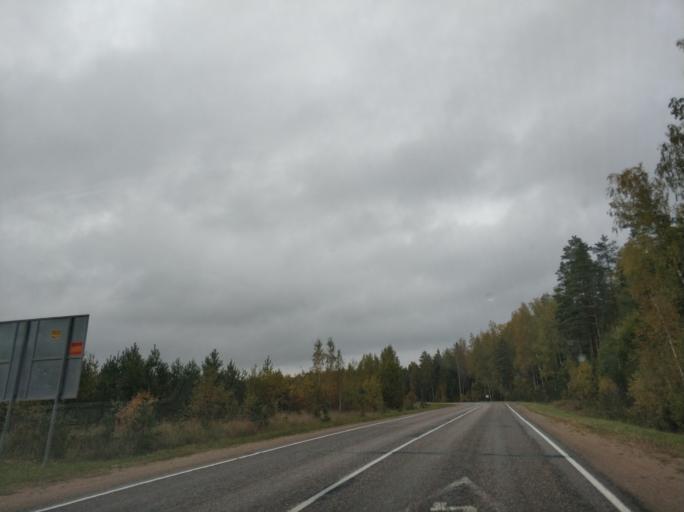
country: RU
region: Pskov
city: Opochka
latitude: 56.5083
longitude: 28.6641
